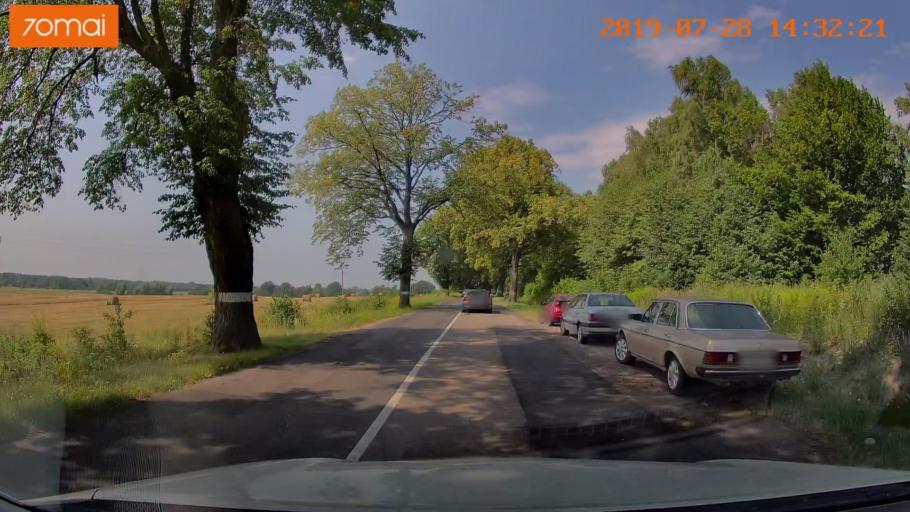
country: RU
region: Kaliningrad
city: Primorsk
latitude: 54.8121
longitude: 20.0424
